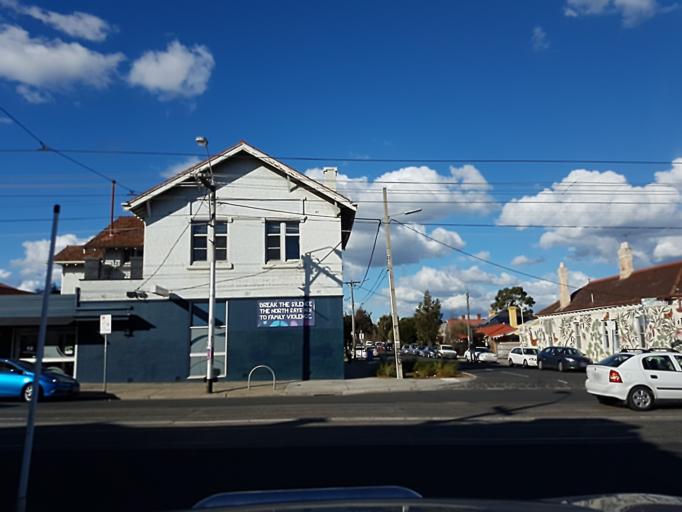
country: AU
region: Victoria
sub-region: Darebin
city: Thornbury
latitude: -37.7587
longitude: 145.0004
